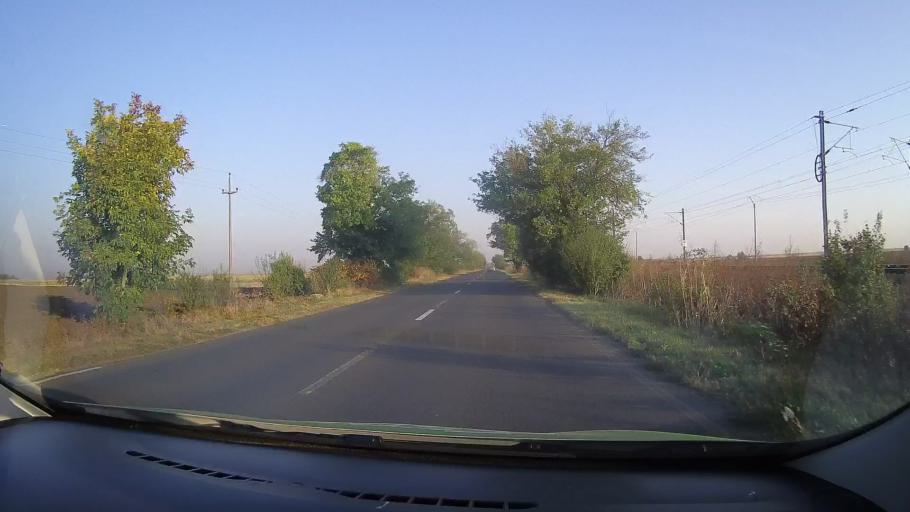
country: RO
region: Arad
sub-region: Comuna Sofronea
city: Sofronea
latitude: 46.2889
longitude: 21.3123
